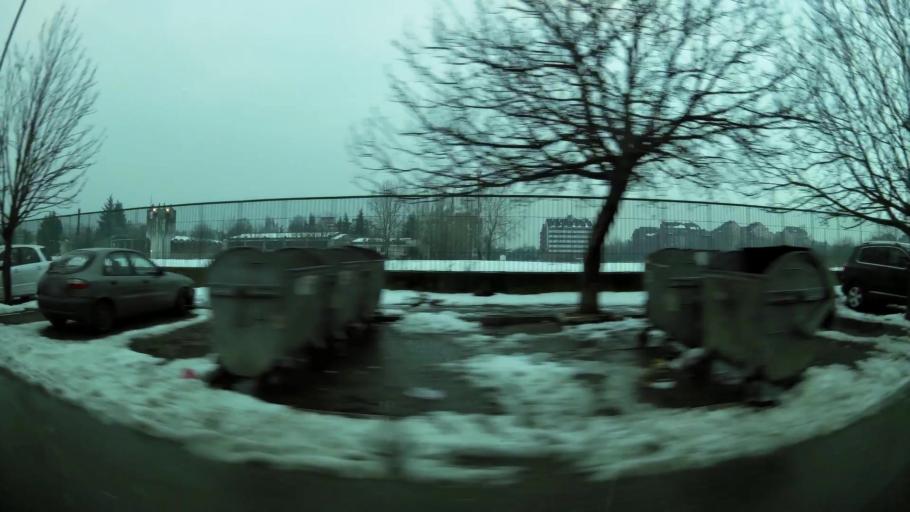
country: RS
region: Central Serbia
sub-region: Belgrade
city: Zemun
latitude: 44.8167
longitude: 20.3789
